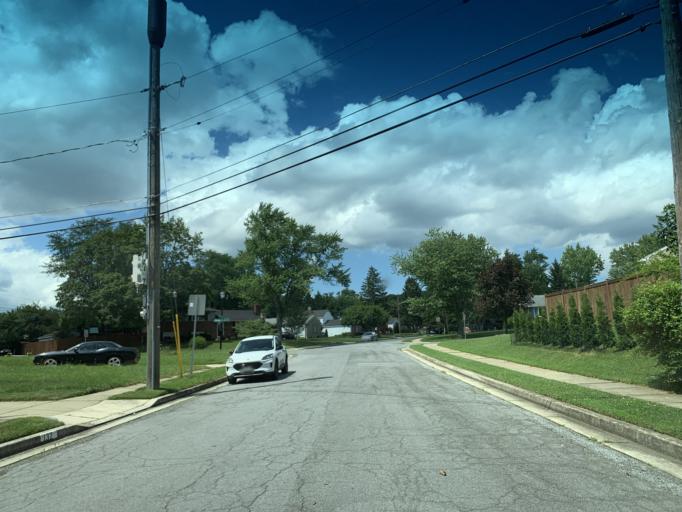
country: US
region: Maryland
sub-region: Baltimore County
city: Timonium
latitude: 39.4429
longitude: -76.6182
